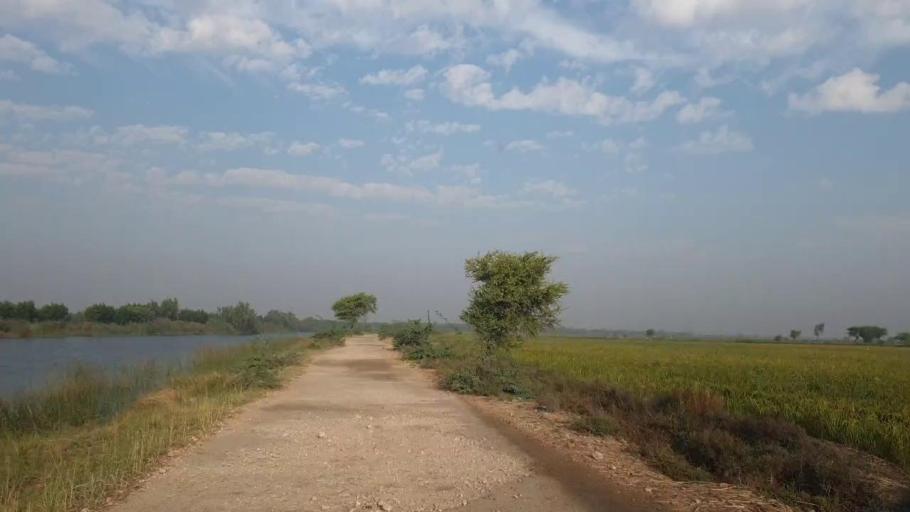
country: PK
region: Sindh
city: Tando Bago
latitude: 24.8157
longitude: 68.9557
